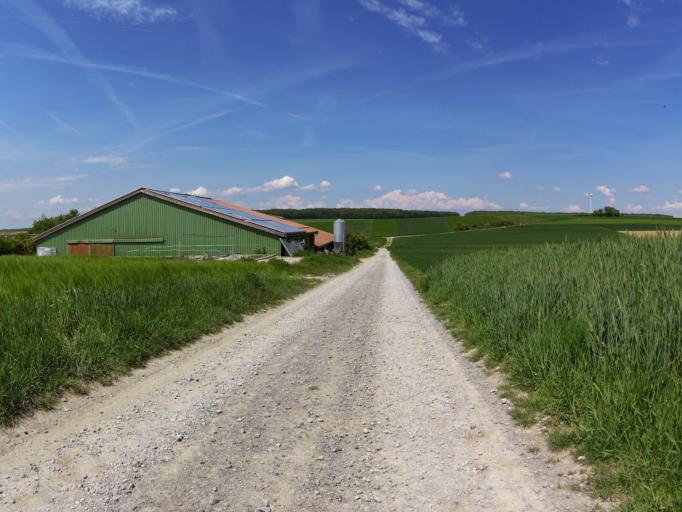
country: DE
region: Bavaria
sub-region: Regierungsbezirk Unterfranken
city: Theilheim
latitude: 49.7321
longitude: 10.0413
